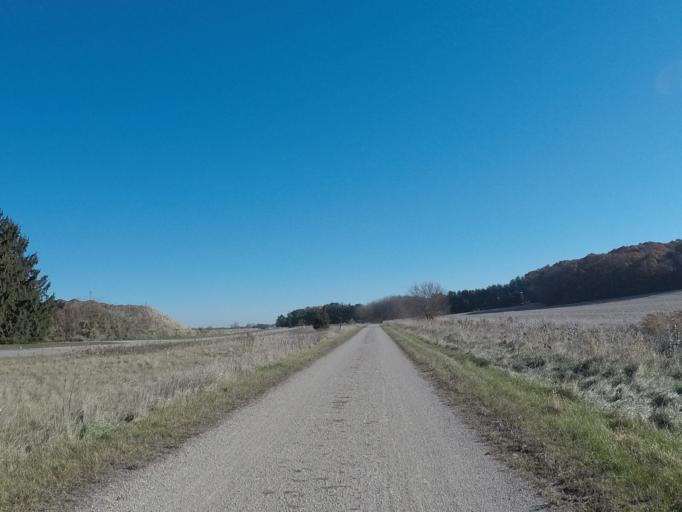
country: US
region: Wisconsin
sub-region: Jefferson County
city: Lake Mills
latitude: 43.0652
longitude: -88.9596
